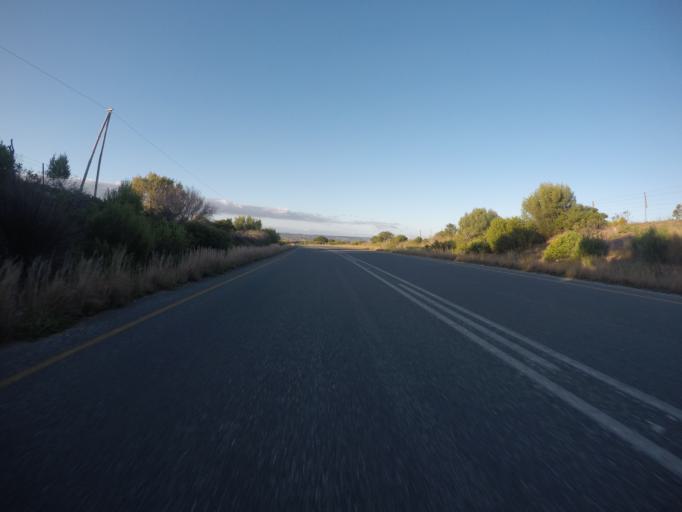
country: ZA
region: Western Cape
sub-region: Eden District Municipality
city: Riversdale
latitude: -34.3929
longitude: 21.3943
